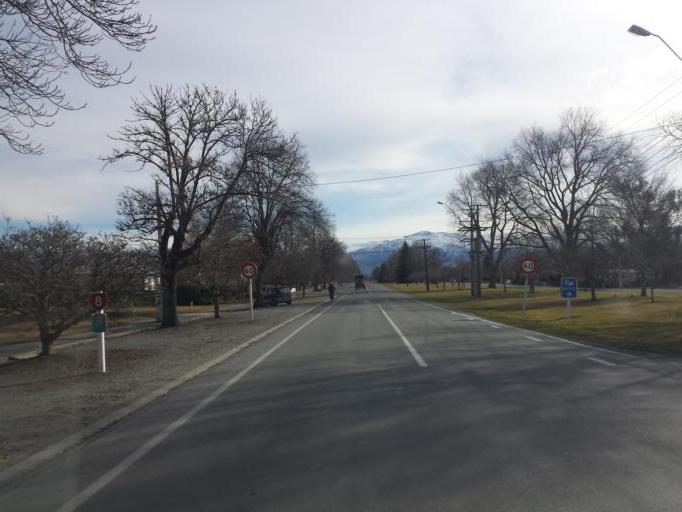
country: NZ
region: Canterbury
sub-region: Timaru District
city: Pleasant Point
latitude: -44.0963
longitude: 170.8272
